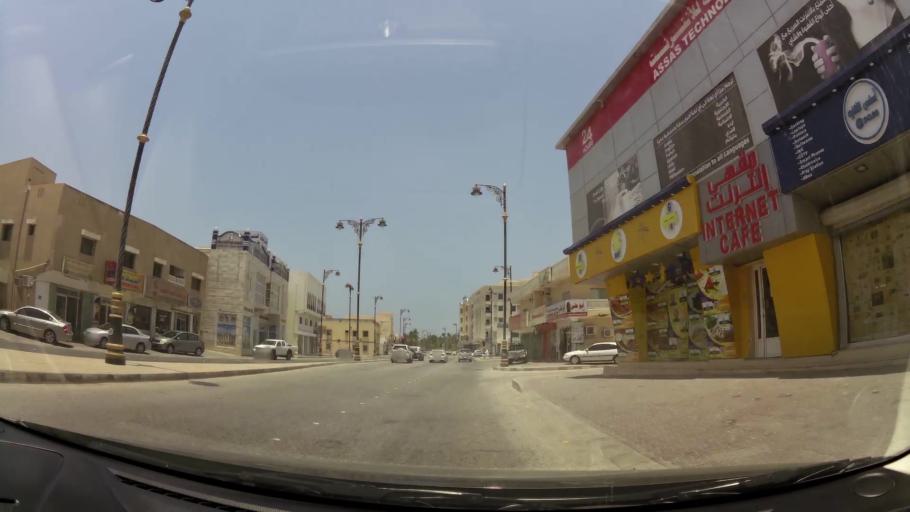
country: OM
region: Zufar
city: Salalah
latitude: 17.0159
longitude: 54.1095
